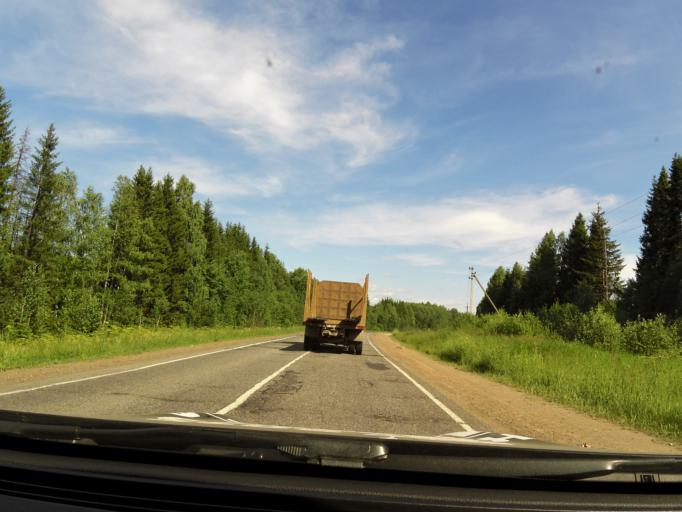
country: RU
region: Kirov
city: Belaya Kholunitsa
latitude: 58.8489
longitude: 50.7551
